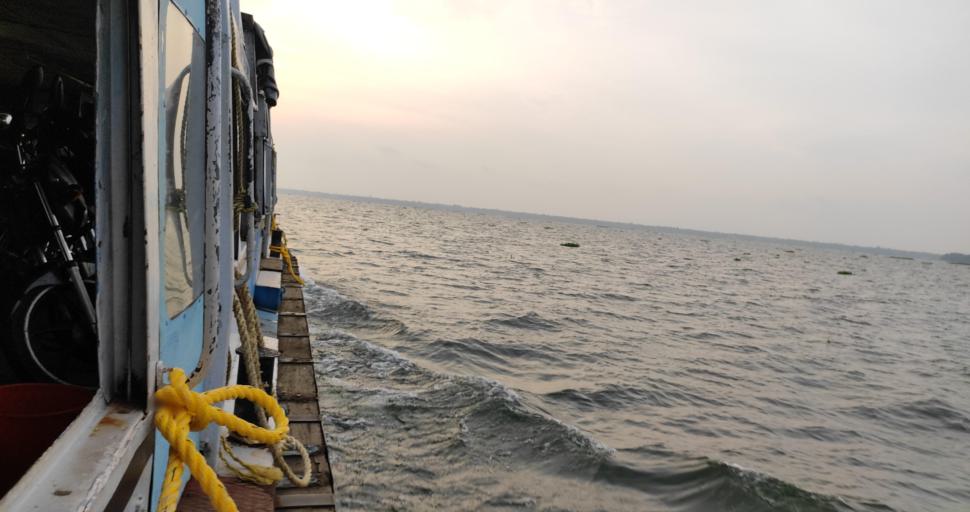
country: IN
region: Kerala
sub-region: Alappuzha
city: Shertallai
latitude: 9.6030
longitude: 76.3950
